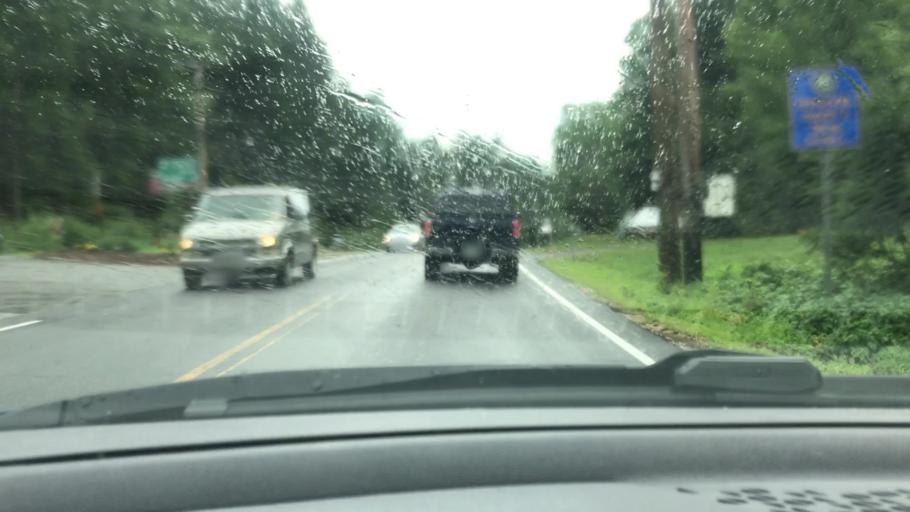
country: US
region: New Hampshire
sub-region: Rockingham County
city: Candia
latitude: 43.1421
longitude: -71.2346
